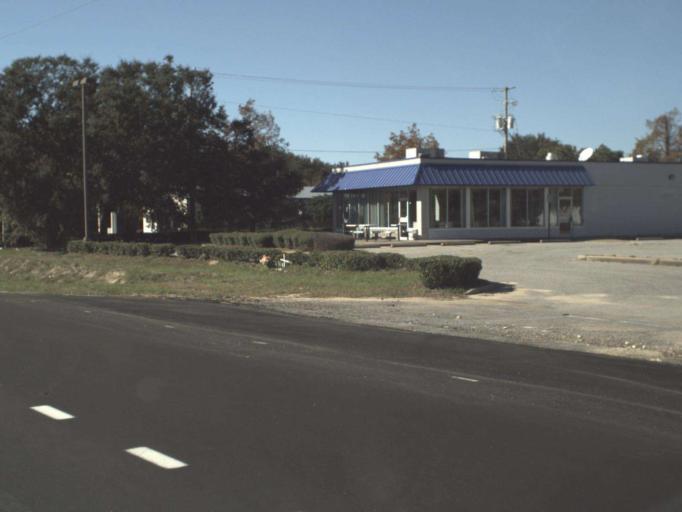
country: US
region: Florida
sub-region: Santa Rosa County
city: Oriole Beach
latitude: 30.3876
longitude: -87.0822
